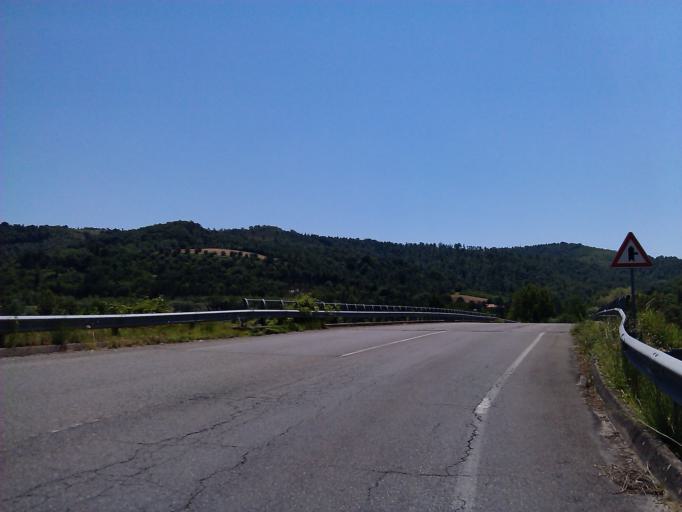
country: IT
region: Umbria
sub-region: Provincia di Terni
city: Fabro Scalo
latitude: 42.8687
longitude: 12.0462
